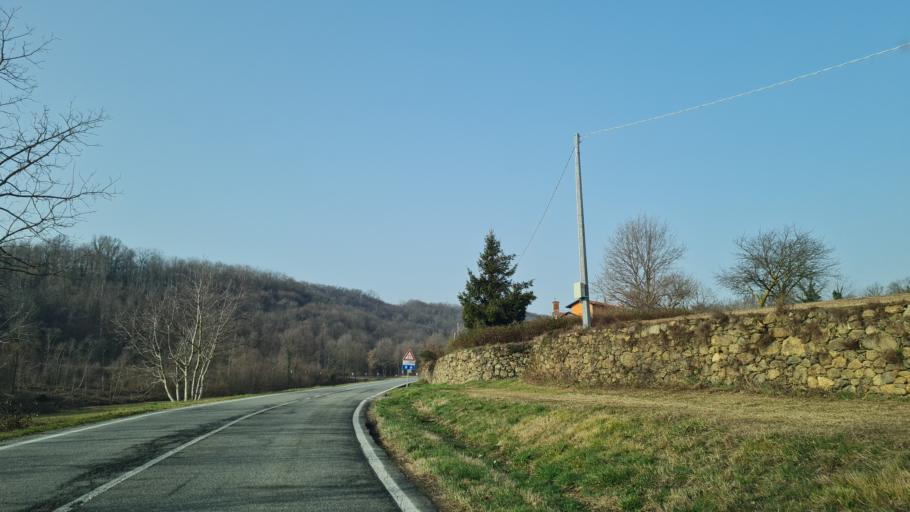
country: IT
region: Piedmont
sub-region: Provincia di Biella
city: Zimone
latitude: 45.4550
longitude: 8.0393
